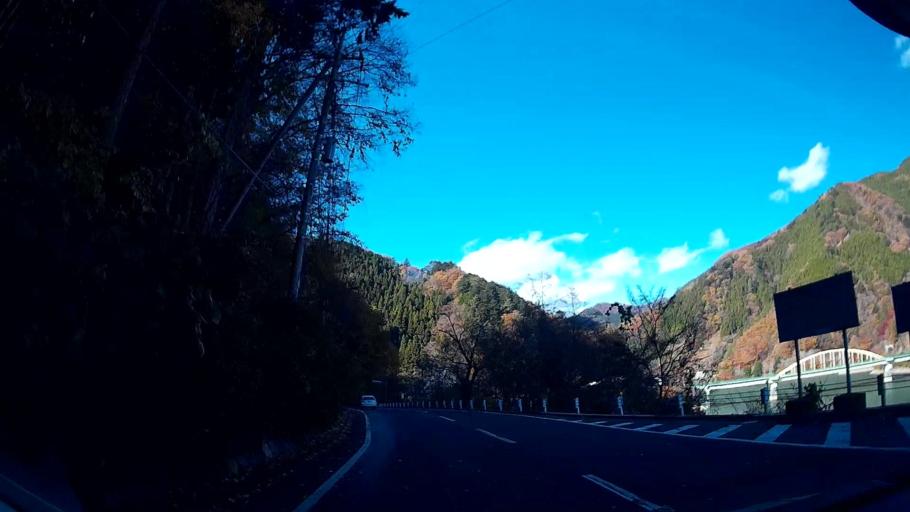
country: JP
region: Yamanashi
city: Otsuki
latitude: 35.7720
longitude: 139.0011
